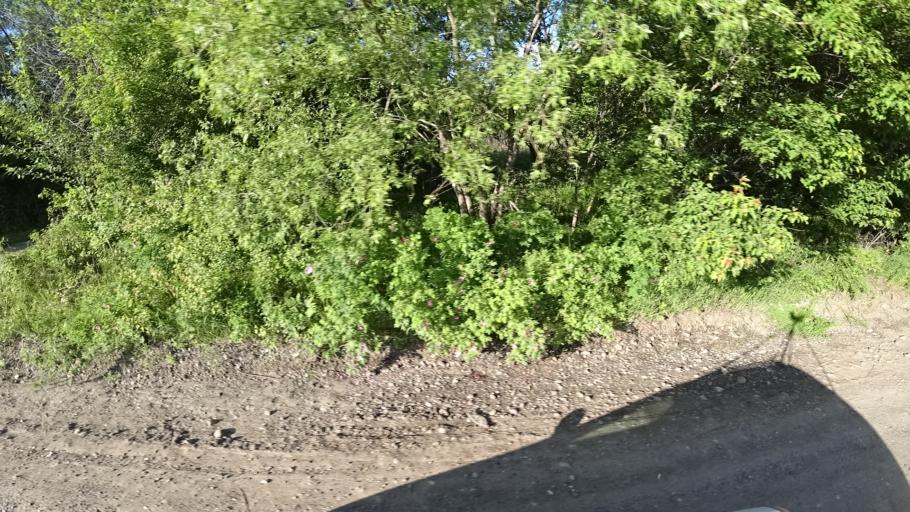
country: RU
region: Khabarovsk Krai
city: Khor
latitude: 47.8534
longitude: 134.9440
